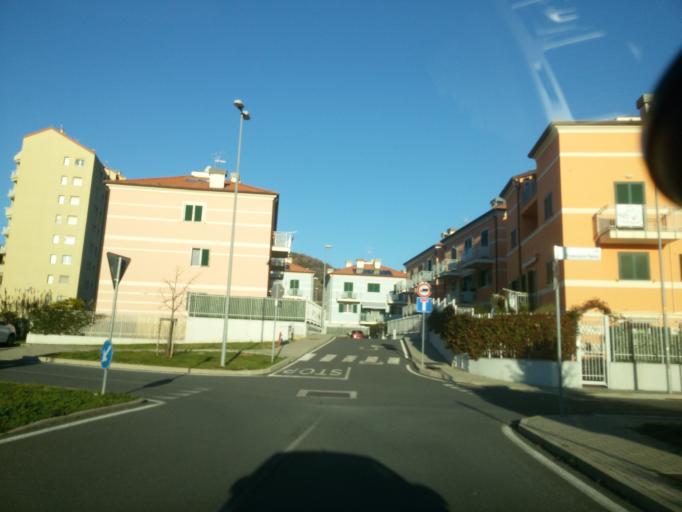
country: IT
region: Liguria
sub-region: Provincia di Savona
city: Valleggia
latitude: 44.2949
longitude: 8.4493
